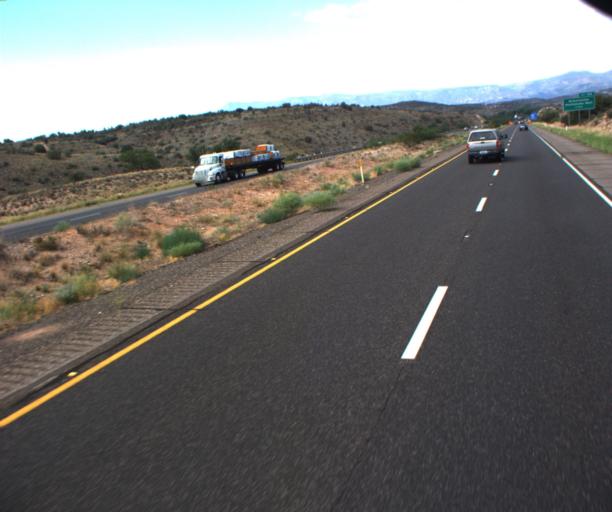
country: US
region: Arizona
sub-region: Yavapai County
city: Lake Montezuma
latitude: 34.6482
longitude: -111.8022
